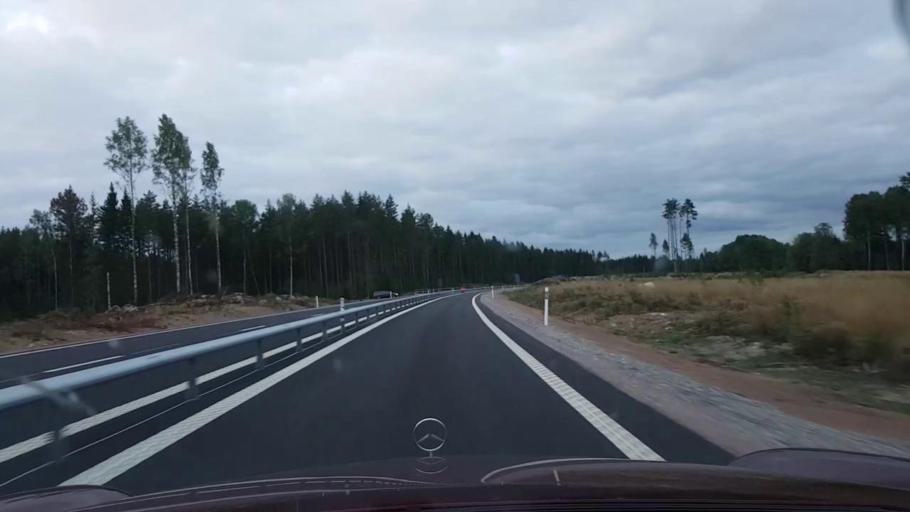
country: SE
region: Vaestmanland
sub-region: Hallstahammars Kommun
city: Hallstahammar
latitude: 59.6548
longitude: 16.2039
